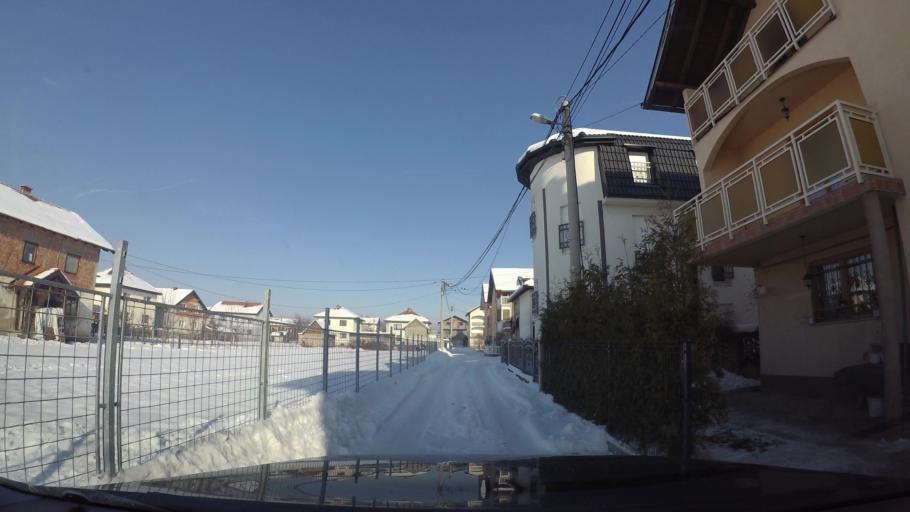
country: BA
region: Federation of Bosnia and Herzegovina
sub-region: Kanton Sarajevo
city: Sarajevo
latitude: 43.8192
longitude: 18.3182
